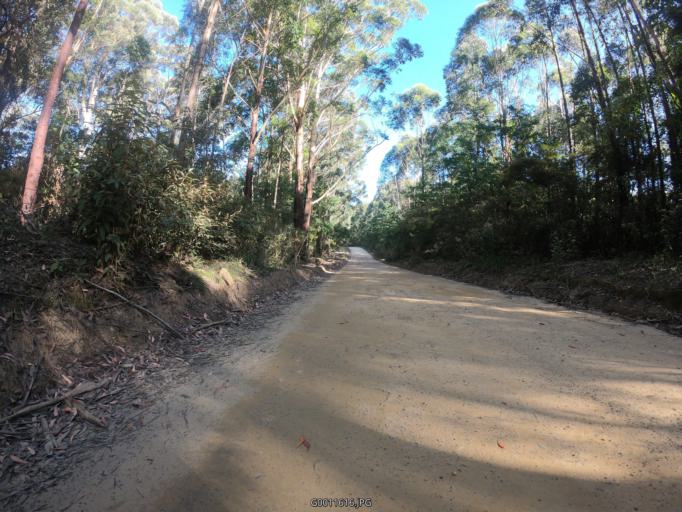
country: AU
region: New South Wales
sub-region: Lake Macquarie Shire
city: Cooranbong
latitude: -33.0457
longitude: 151.3078
